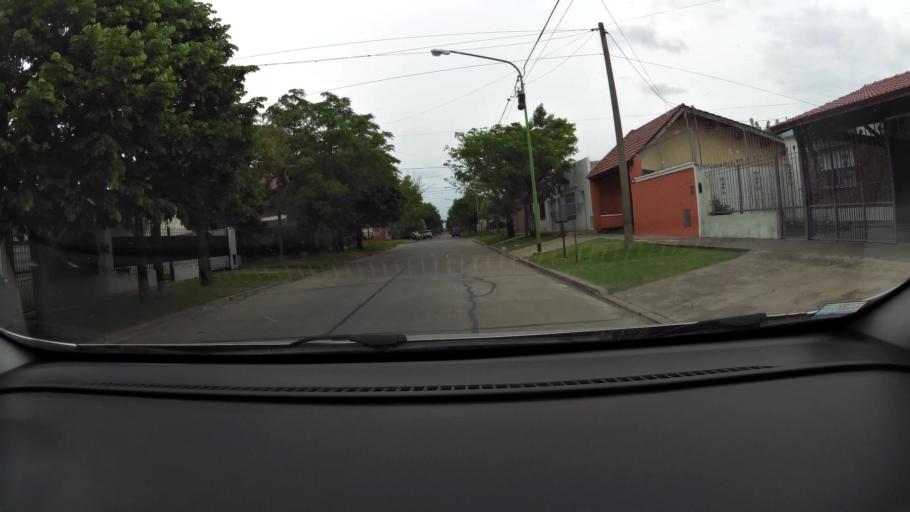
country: AR
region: Buenos Aires
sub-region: Partido de Campana
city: Campana
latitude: -34.1773
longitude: -58.9560
